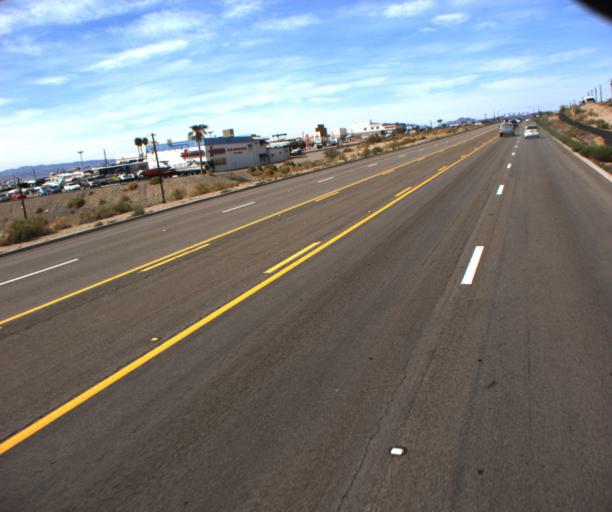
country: US
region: Arizona
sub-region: Mohave County
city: Lake Havasu City
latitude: 34.4889
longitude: -114.3493
